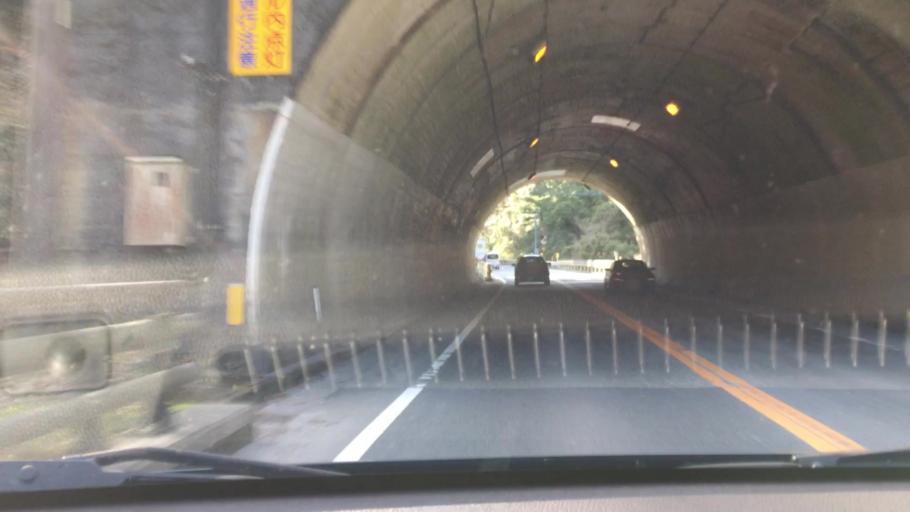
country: JP
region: Oita
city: Tsukumiura
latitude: 33.0030
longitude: 131.7924
